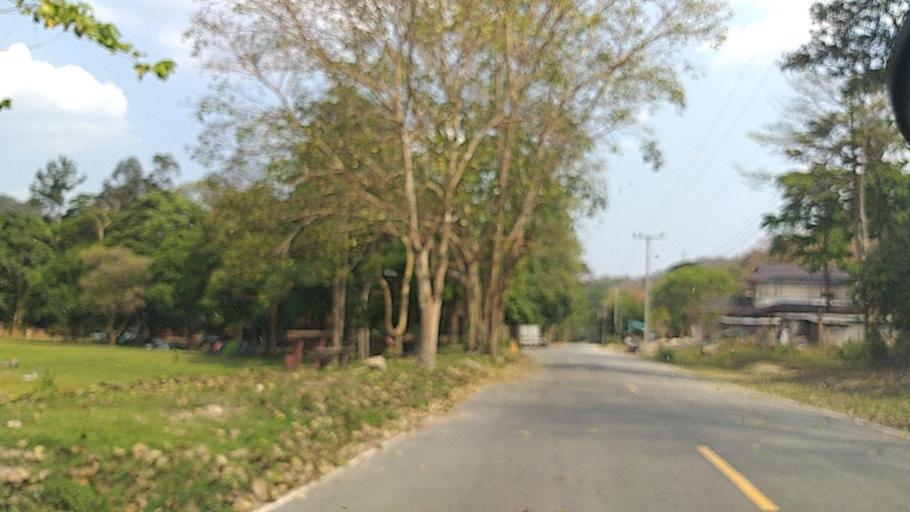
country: TH
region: Sara Buri
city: Wihan Daeng
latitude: 14.4417
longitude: 100.9591
